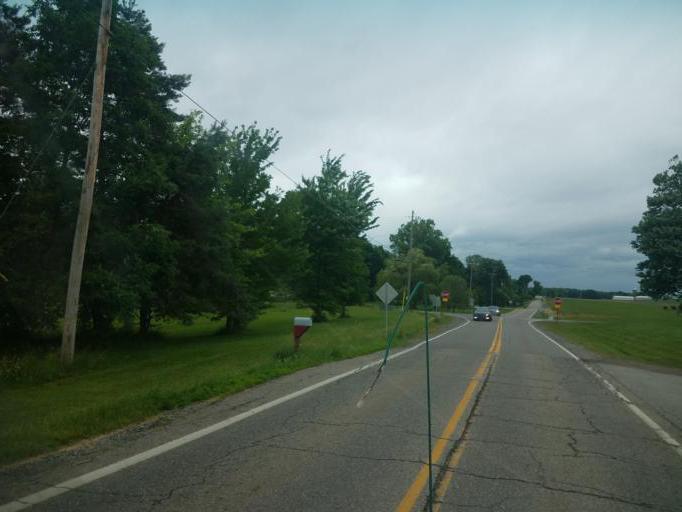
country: US
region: Ohio
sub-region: Columbiana County
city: Leetonia
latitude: 40.8427
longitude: -80.7358
